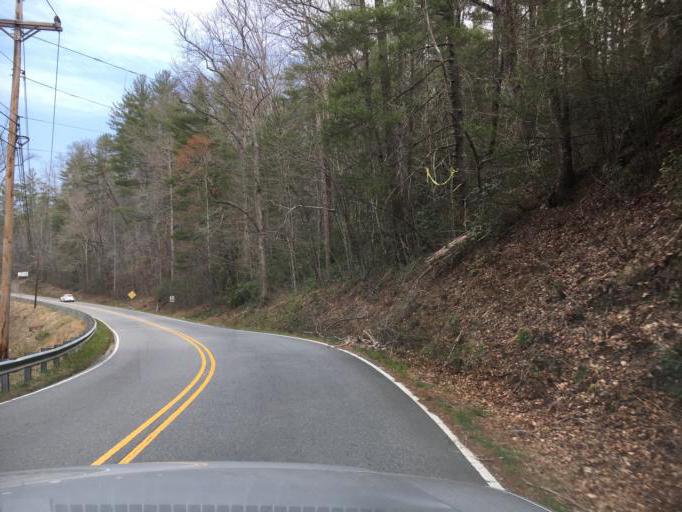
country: US
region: North Carolina
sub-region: Rutherford County
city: Lake Lure
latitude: 35.4226
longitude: -82.1687
